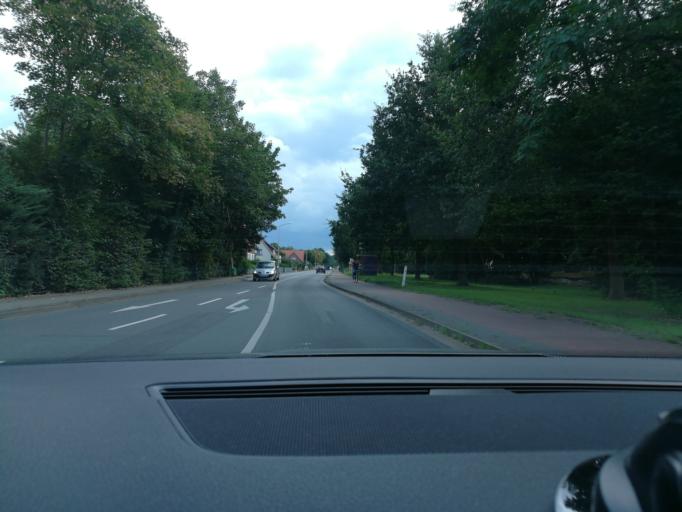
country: DE
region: North Rhine-Westphalia
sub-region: Regierungsbezirk Detmold
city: Minden
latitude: 52.3214
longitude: 8.8725
